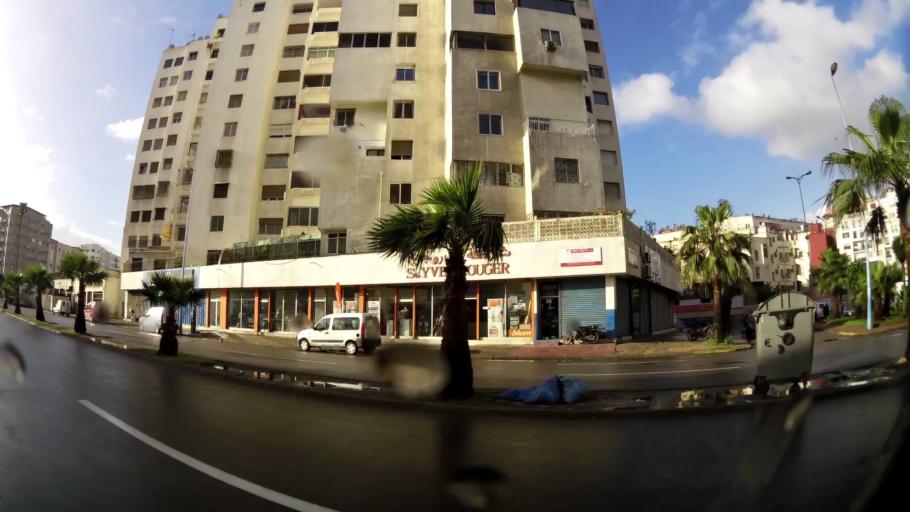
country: MA
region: Grand Casablanca
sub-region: Casablanca
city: Casablanca
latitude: 33.5889
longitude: -7.6014
